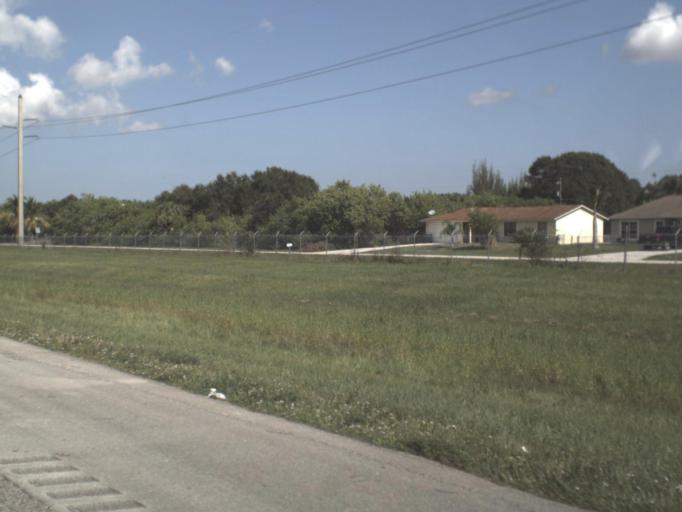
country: US
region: Florida
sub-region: Saint Lucie County
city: River Park
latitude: 27.3248
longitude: -80.3742
